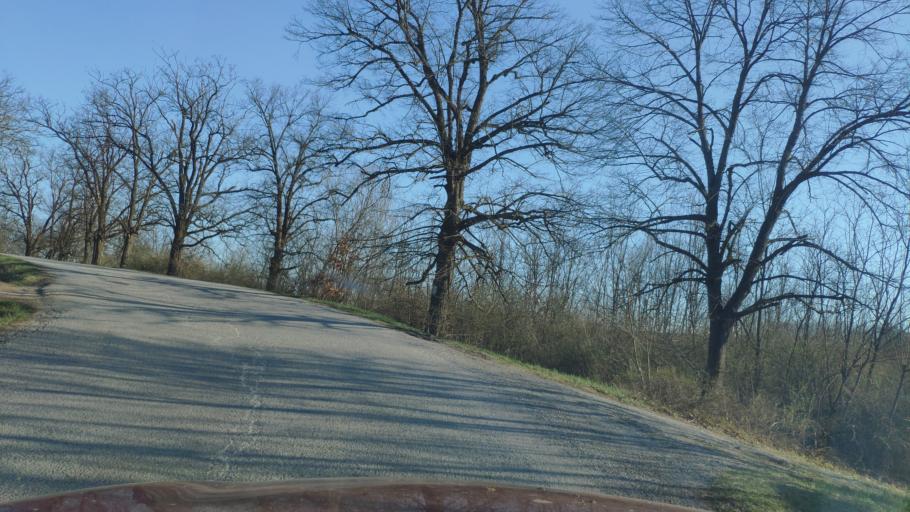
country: SK
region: Banskobystricky
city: Revuca
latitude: 48.5000
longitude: 20.2547
